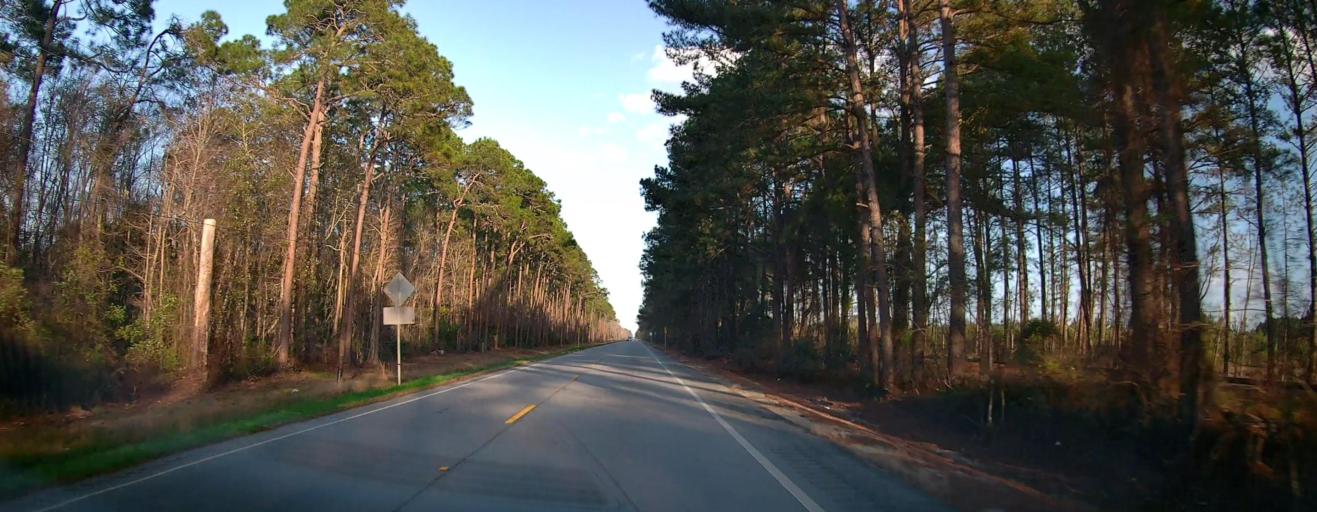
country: US
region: Georgia
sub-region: Bryan County
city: Pembroke
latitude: 32.1410
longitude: -81.6984
